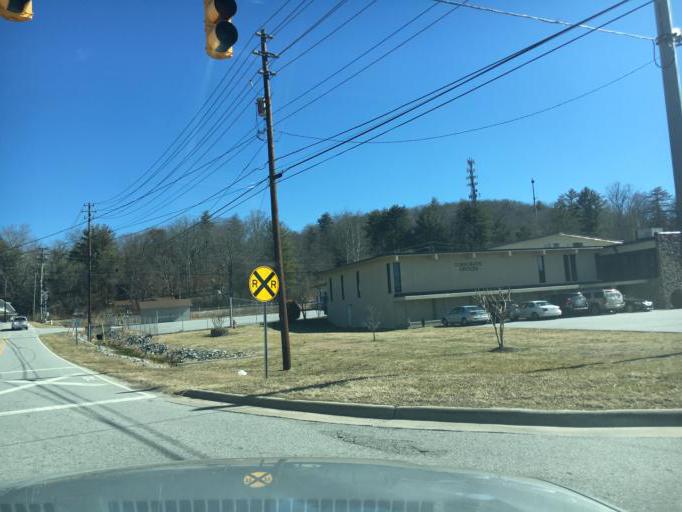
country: US
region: North Carolina
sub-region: Henderson County
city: Mountain Home
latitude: 35.3924
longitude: -82.5024
